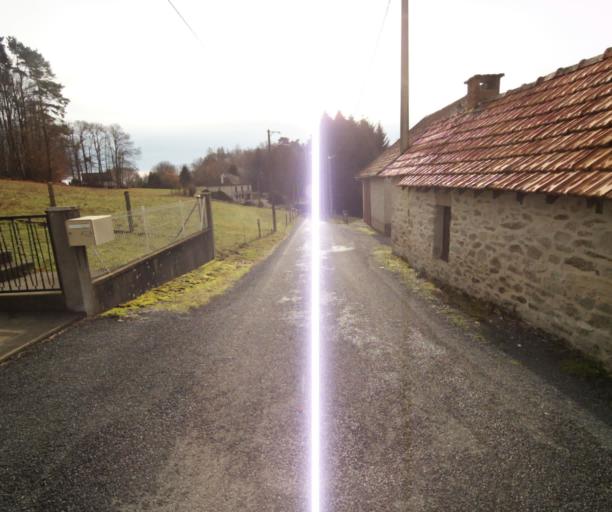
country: FR
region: Limousin
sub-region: Departement de la Correze
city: Chameyrat
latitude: 45.2690
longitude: 1.6867
